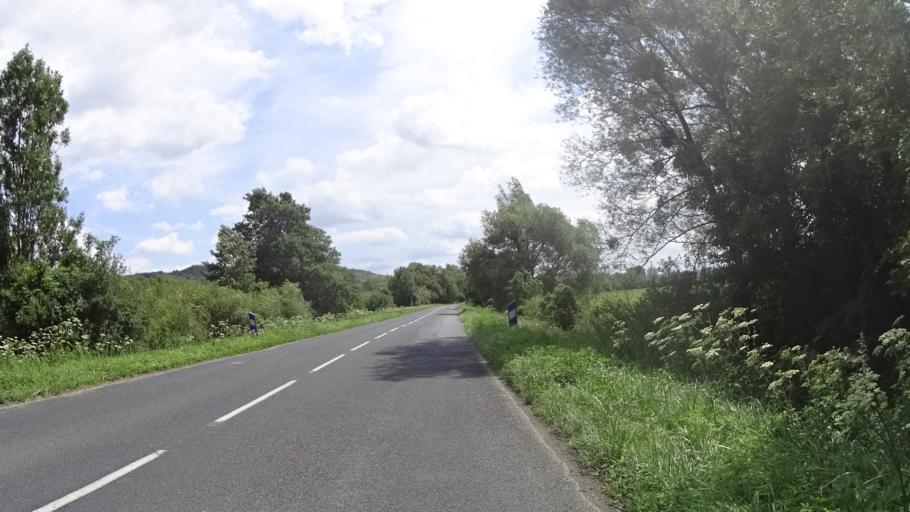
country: FR
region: Lorraine
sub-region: Departement de la Meuse
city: Euville
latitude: 48.7330
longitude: 5.6630
